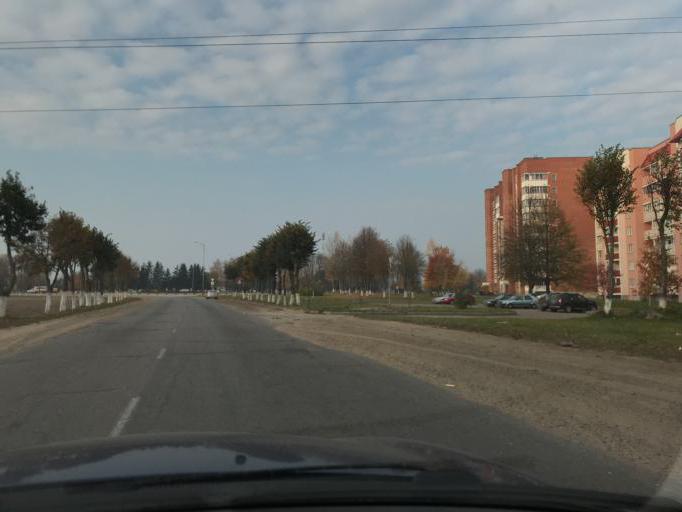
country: BY
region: Grodnenskaya
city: Lida
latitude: 53.8745
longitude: 25.2751
